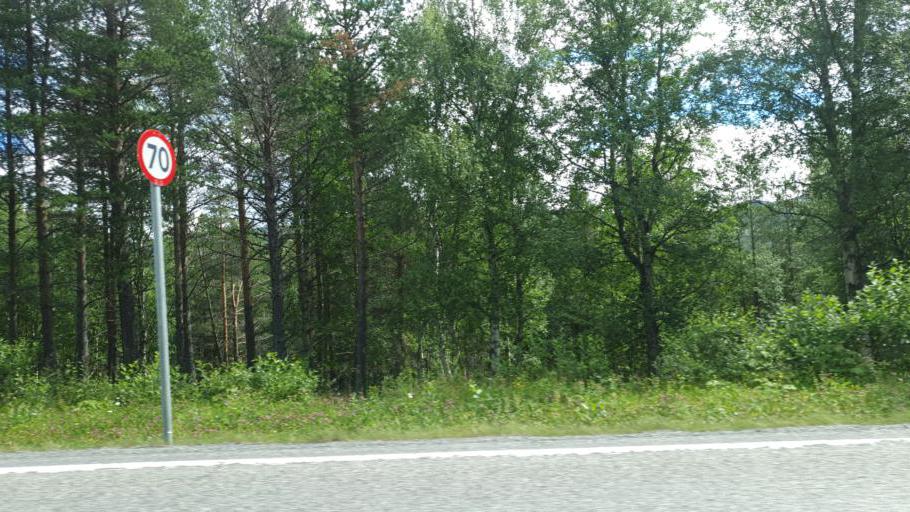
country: NO
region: Sor-Trondelag
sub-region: Rennebu
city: Berkak
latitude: 62.6722
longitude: 9.9107
